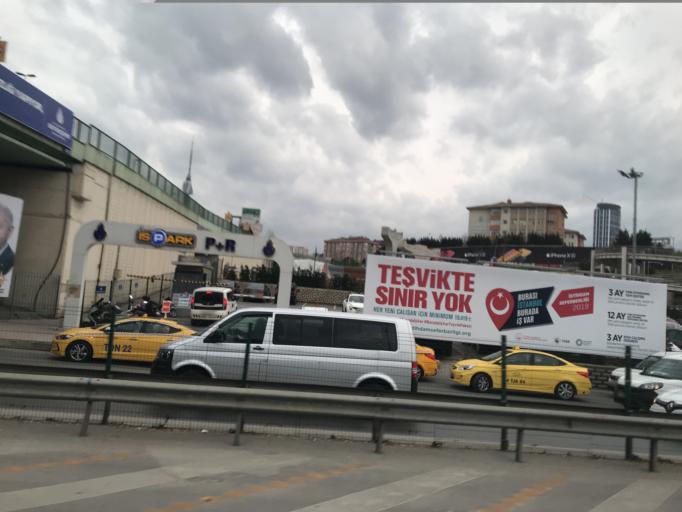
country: TR
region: Istanbul
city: UEskuedar
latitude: 40.9987
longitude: 29.0577
